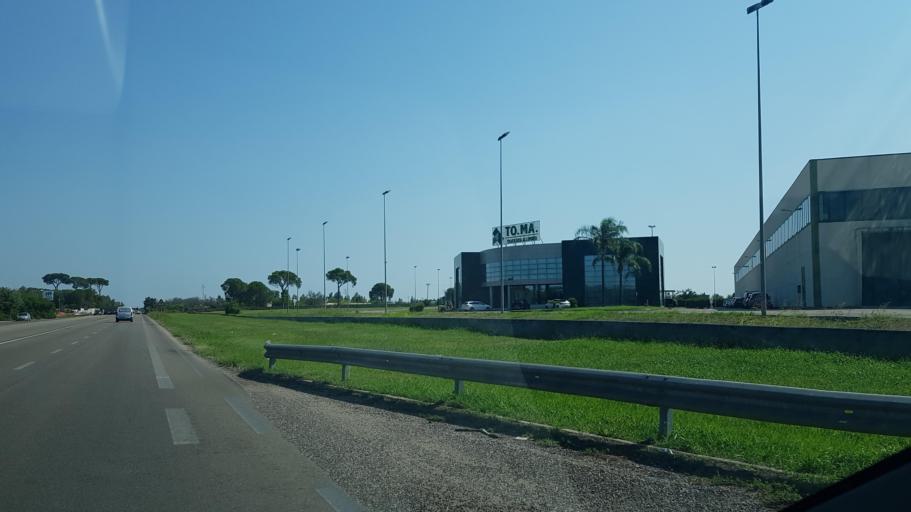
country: IT
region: Apulia
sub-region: Provincia di Lecce
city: Scorrano
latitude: 40.0991
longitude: 18.3146
